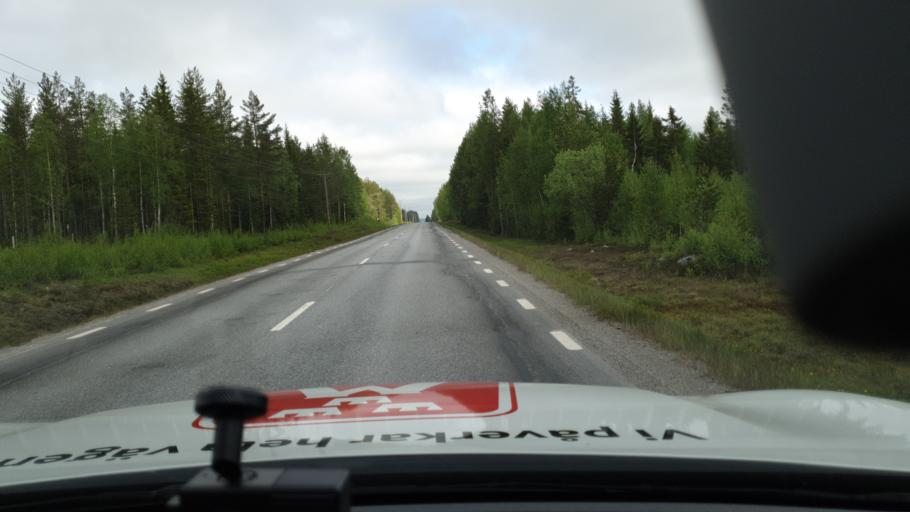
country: SE
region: Vaesterbotten
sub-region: Umea Kommun
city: Roback
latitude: 63.9019
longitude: 20.1983
